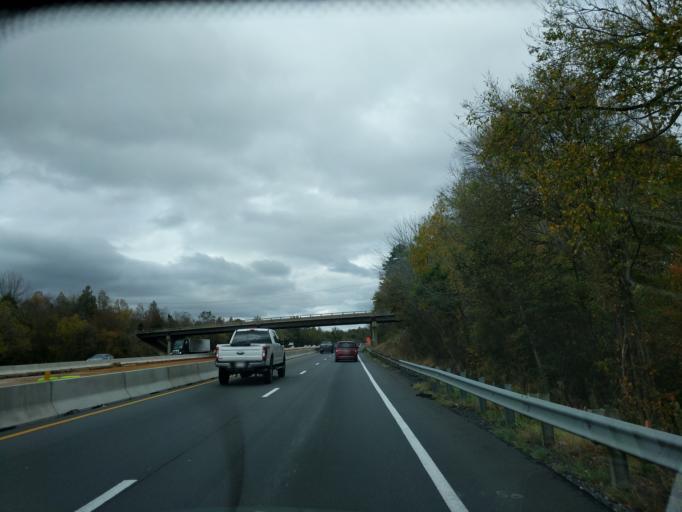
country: US
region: North Carolina
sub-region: Rowan County
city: Landis
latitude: 35.5243
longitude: -80.5719
